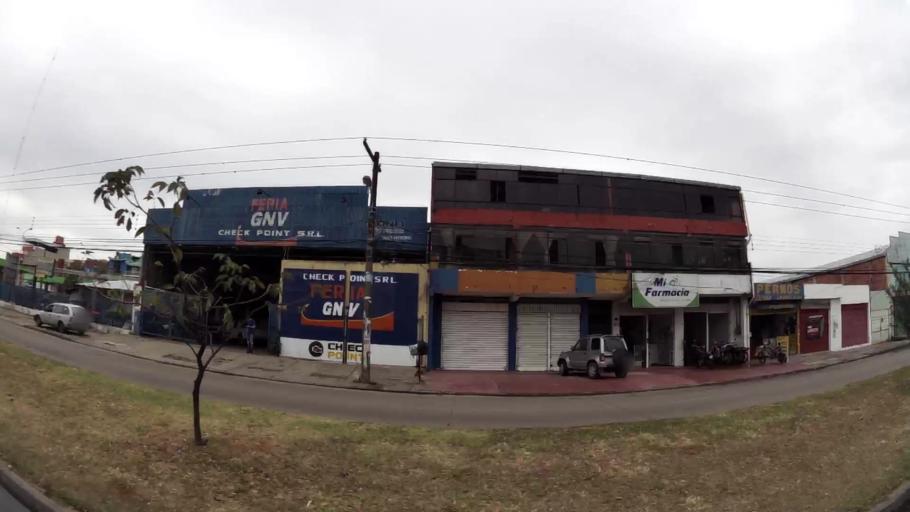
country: BO
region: Santa Cruz
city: Santa Cruz de la Sierra
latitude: -17.7907
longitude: -63.1654
